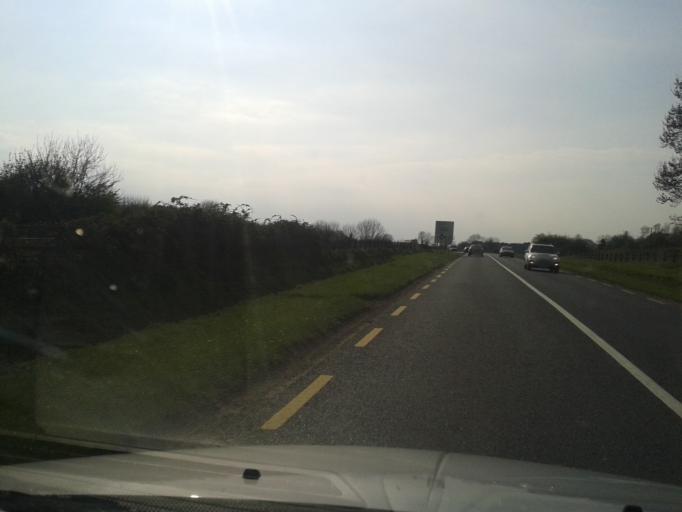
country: IE
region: Leinster
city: Ballymun
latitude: 53.4398
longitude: -6.2579
